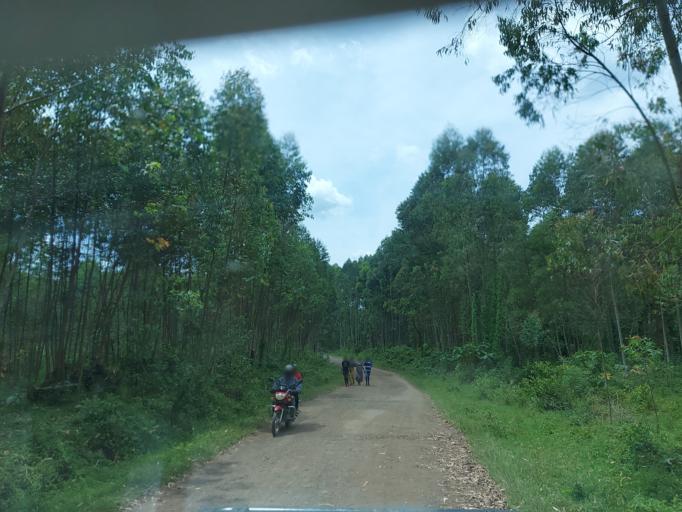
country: CD
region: South Kivu
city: Bukavu
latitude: -2.2454
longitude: 28.8262
